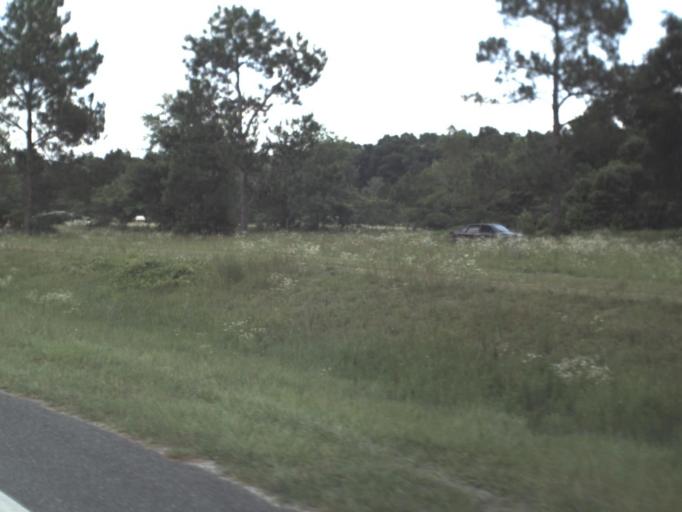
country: US
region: Florida
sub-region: Levy County
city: Manatee Road
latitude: 29.6066
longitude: -82.9234
